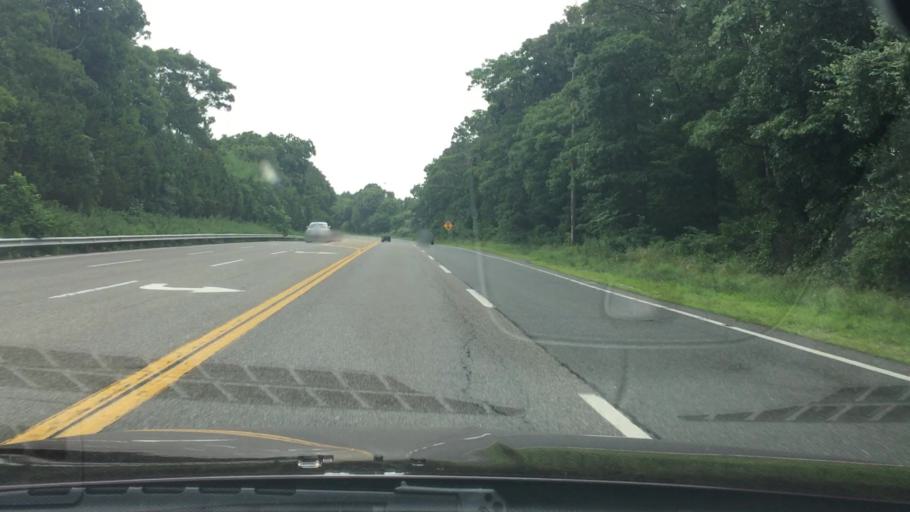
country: US
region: New York
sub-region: Suffolk County
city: Commack
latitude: 40.8108
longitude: -73.2832
